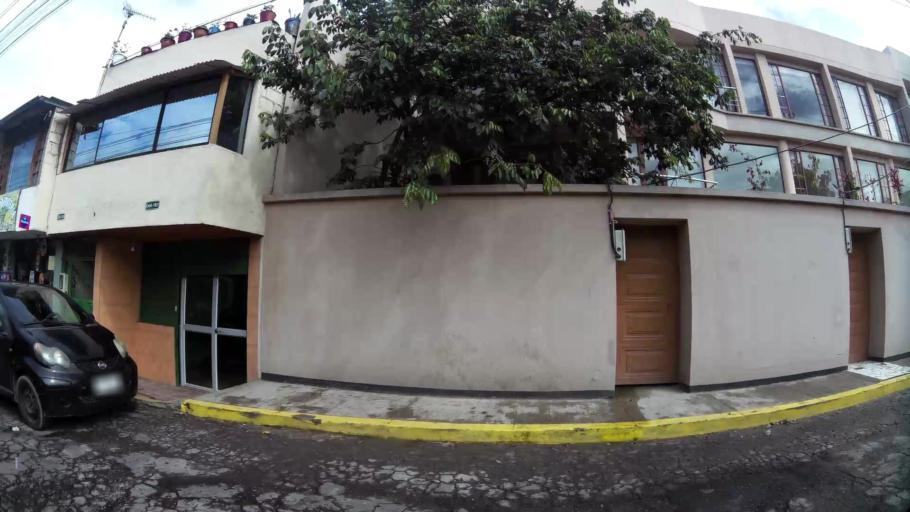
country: EC
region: Pichincha
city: Sangolqui
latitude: -0.3048
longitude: -78.4322
